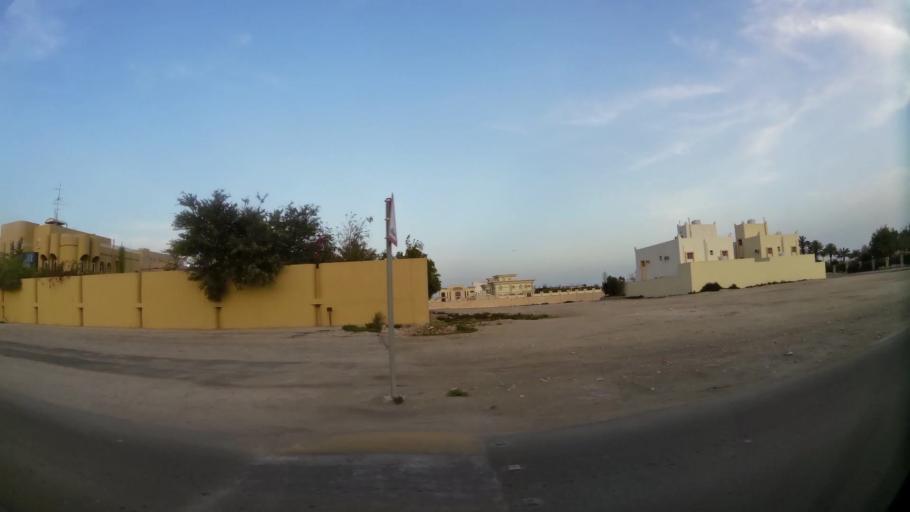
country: QA
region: Al Wakrah
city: Al Wakrah
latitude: 25.1817
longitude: 51.6109
